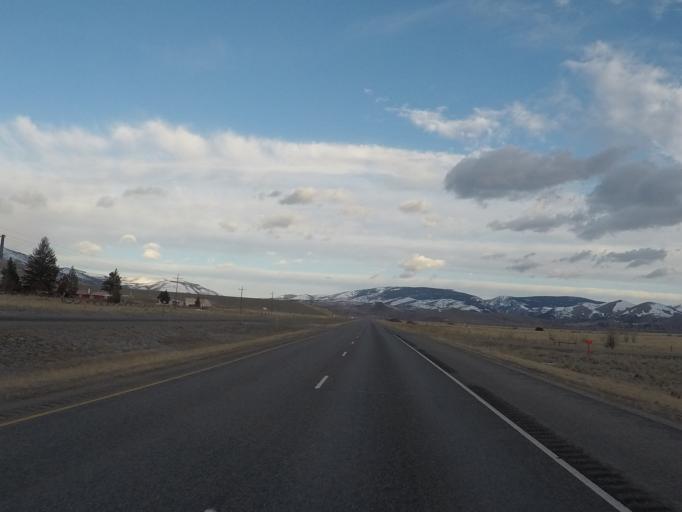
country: US
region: Montana
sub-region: Deer Lodge County
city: Anaconda
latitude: 46.1120
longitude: -112.8590
